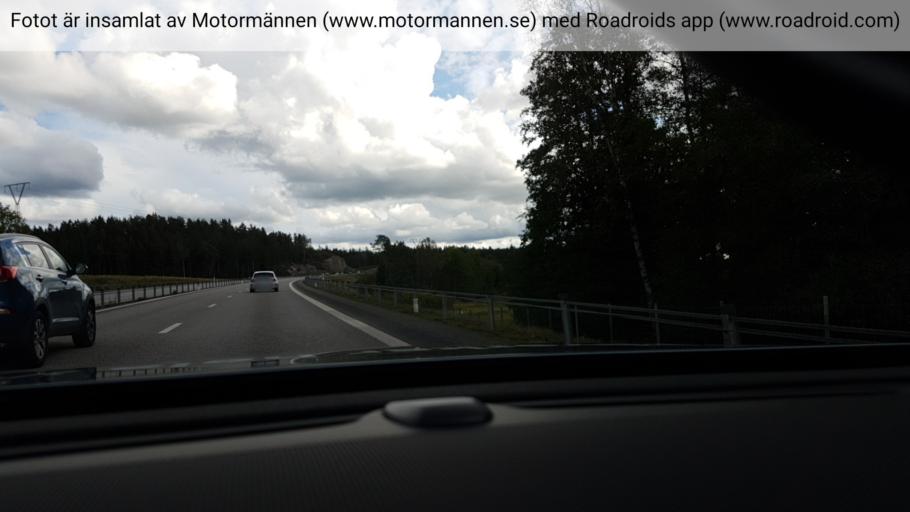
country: SE
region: Vaestra Goetaland
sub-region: Lilla Edets Kommun
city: Lodose
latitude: 58.0652
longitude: 12.1618
